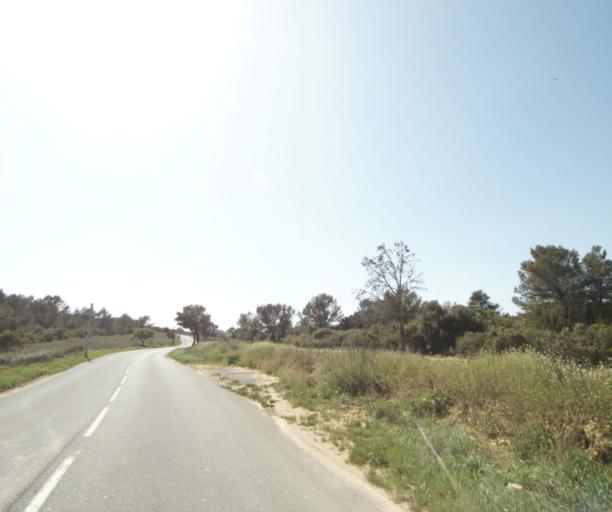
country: FR
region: Languedoc-Roussillon
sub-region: Departement de l'Herault
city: Combaillaux
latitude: 43.6428
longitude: 3.7562
